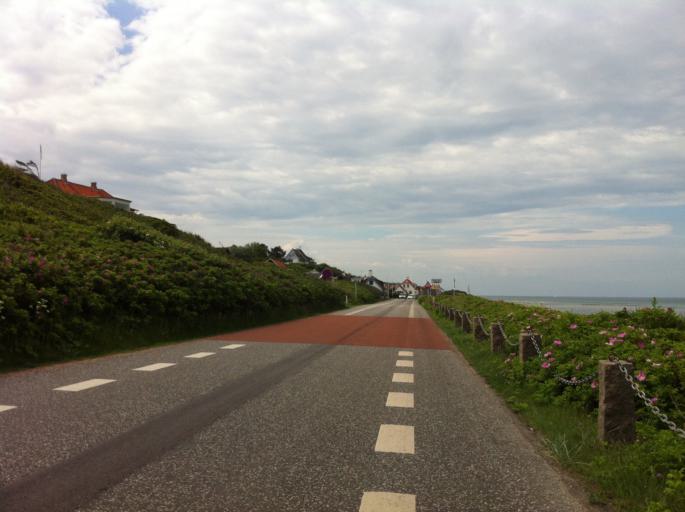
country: DK
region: Capital Region
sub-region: Gribskov Kommune
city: Helsinge
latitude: 56.1006
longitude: 12.1646
